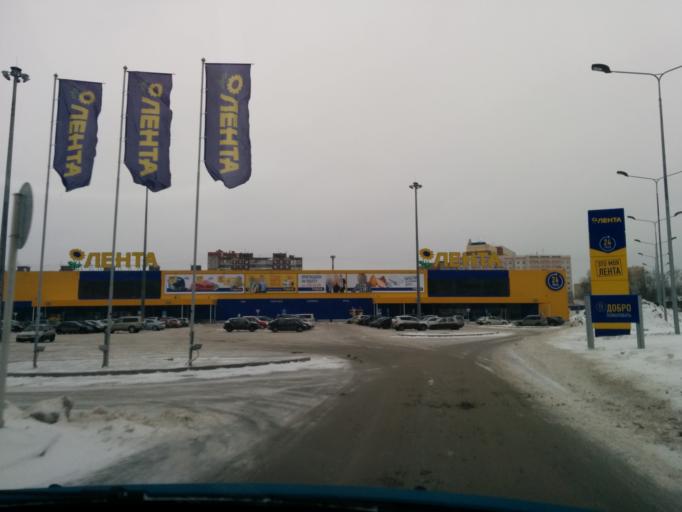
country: RU
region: Perm
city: Kondratovo
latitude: 57.9950
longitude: 56.1743
